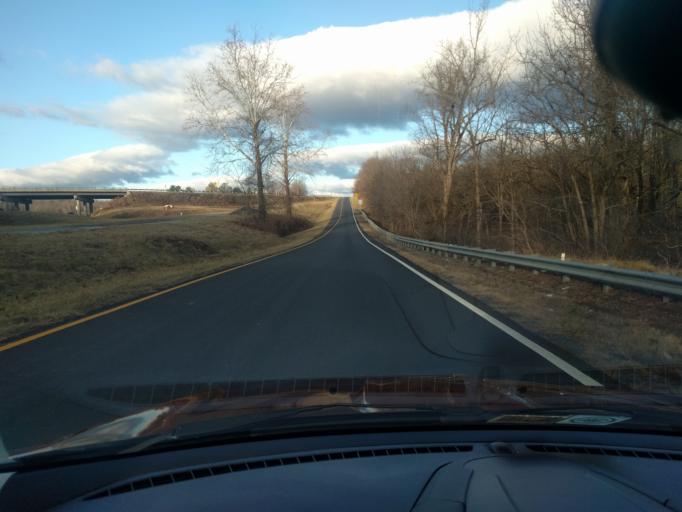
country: US
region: Virginia
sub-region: City of Bedford
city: Bedford
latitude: 37.3361
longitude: -79.5424
